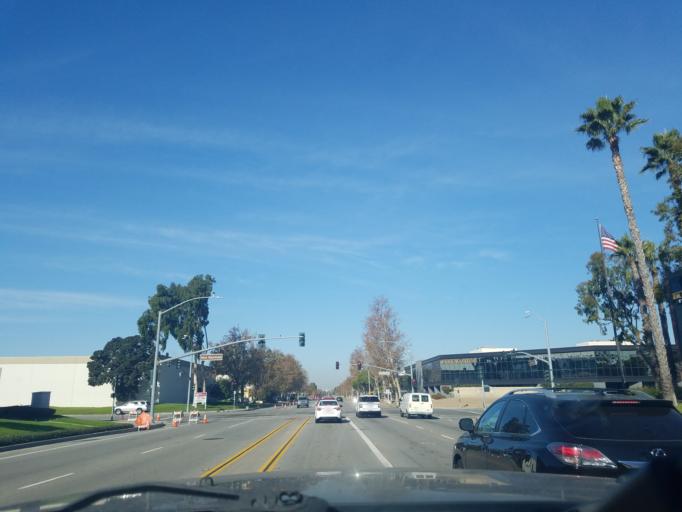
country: US
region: California
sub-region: Orange County
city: Irvine
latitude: 33.6927
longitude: -117.8382
